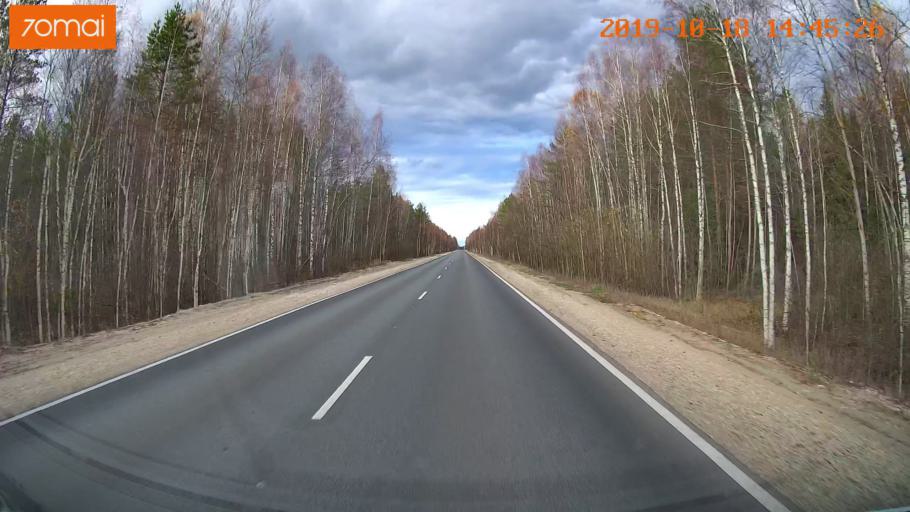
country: RU
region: Vladimir
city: Velikodvorskiy
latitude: 55.3548
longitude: 40.6789
